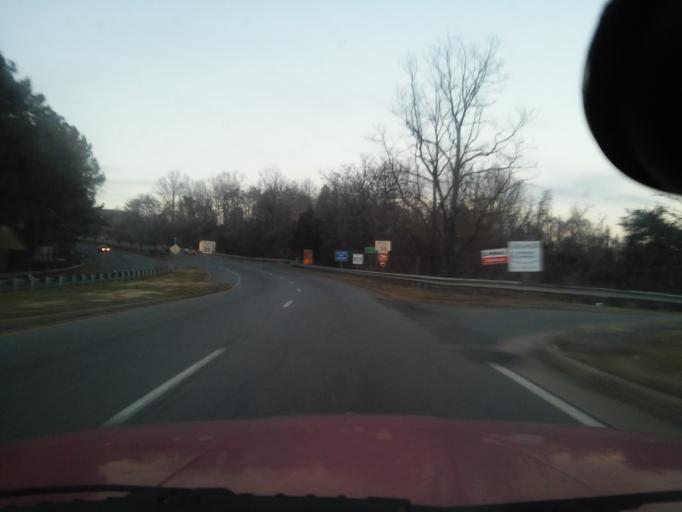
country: US
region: Virginia
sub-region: City of Charlottesville
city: Charlottesville
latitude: 38.0138
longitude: -78.4750
